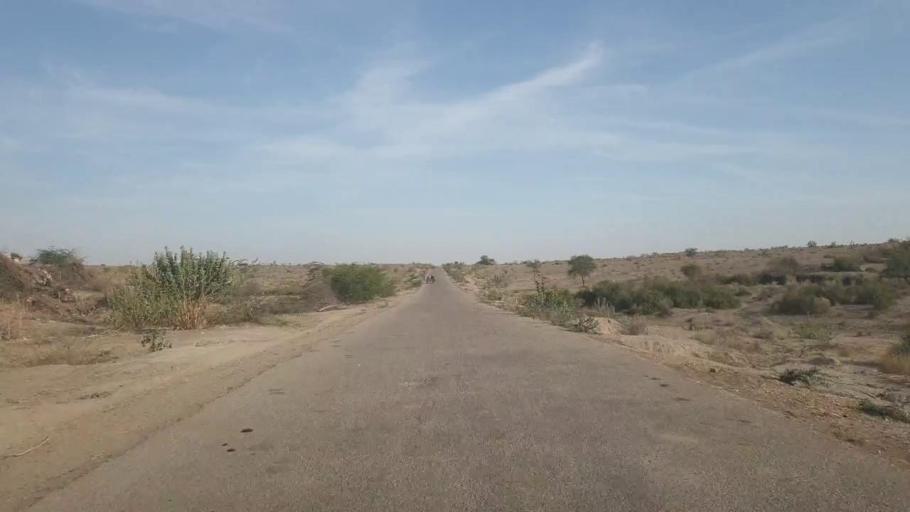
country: PK
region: Sindh
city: Nabisar
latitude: 25.0675
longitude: 69.6486
